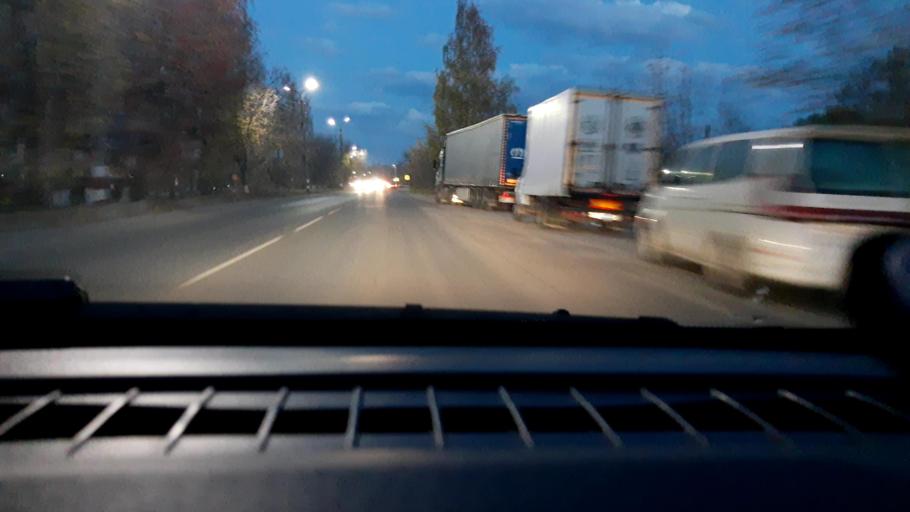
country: RU
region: Nizjnij Novgorod
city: Novaya Balakhna
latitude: 56.4872
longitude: 43.5859
